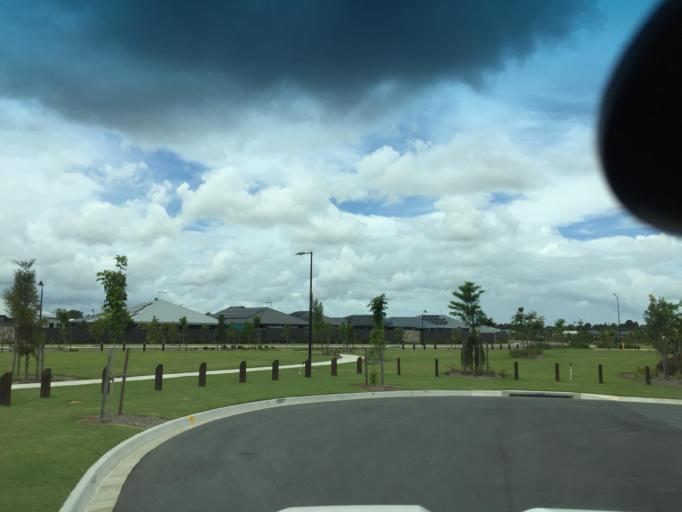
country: AU
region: Queensland
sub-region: Moreton Bay
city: Caboolture
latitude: -27.0626
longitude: 152.9248
